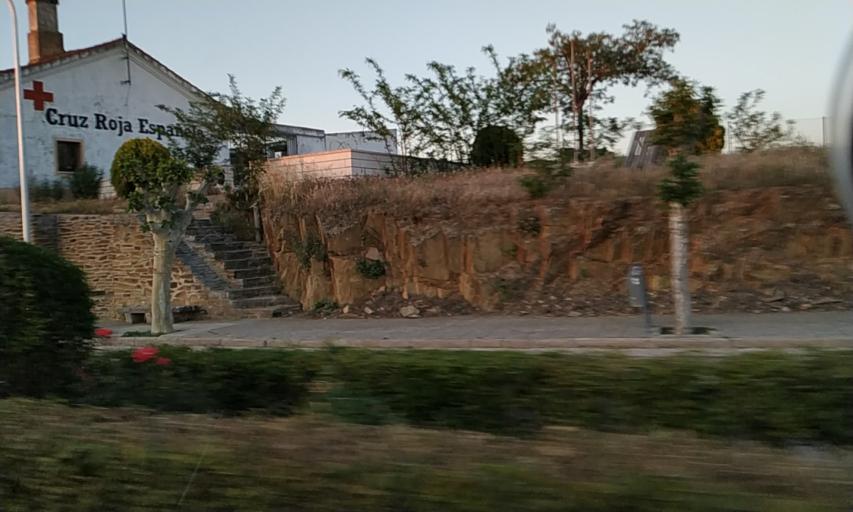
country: ES
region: Extremadura
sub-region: Provincia de Caceres
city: Alcantara
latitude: 39.7101
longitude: -6.8862
